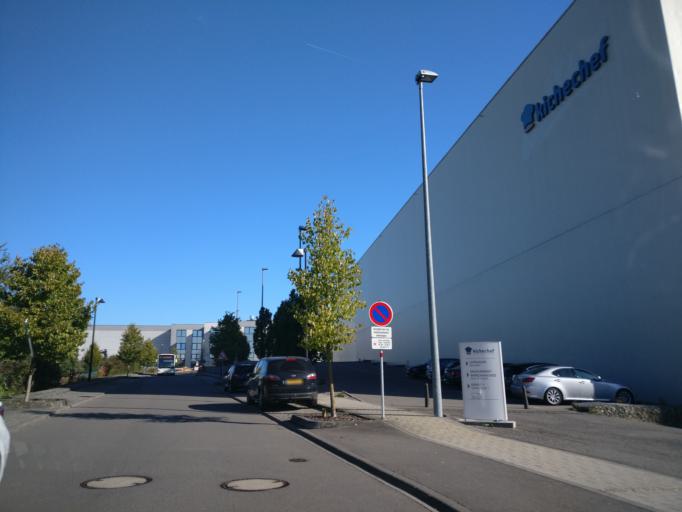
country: LU
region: Luxembourg
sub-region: Canton de Capellen
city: Mamer
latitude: 49.6405
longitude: 6.0116
